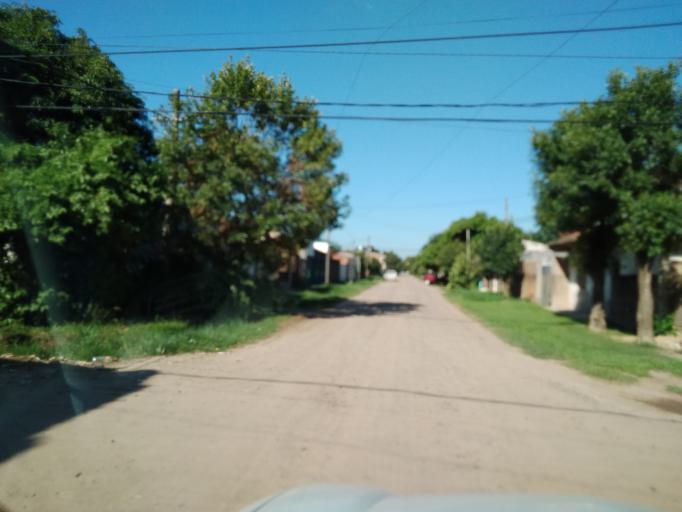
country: AR
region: Corrientes
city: Corrientes
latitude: -27.4848
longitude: -58.8035
